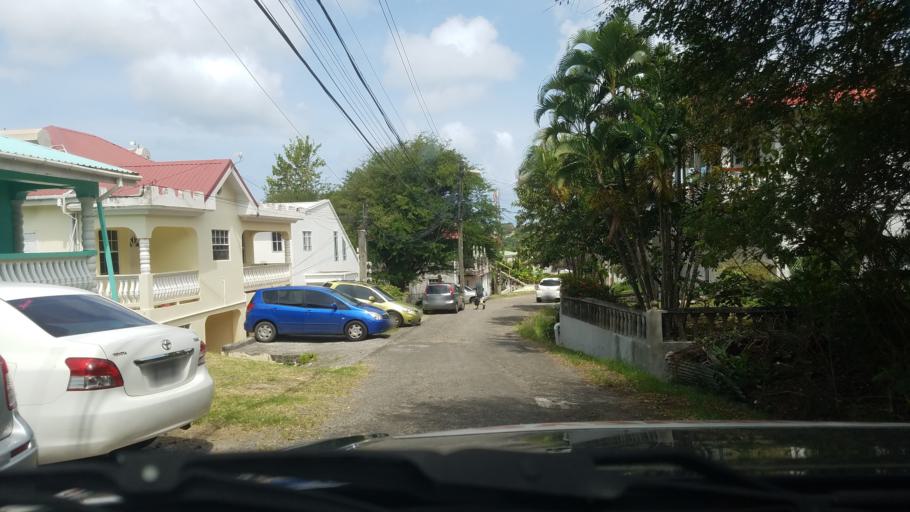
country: LC
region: Gros-Islet
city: Gros Islet
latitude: 14.0457
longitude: -60.9599
